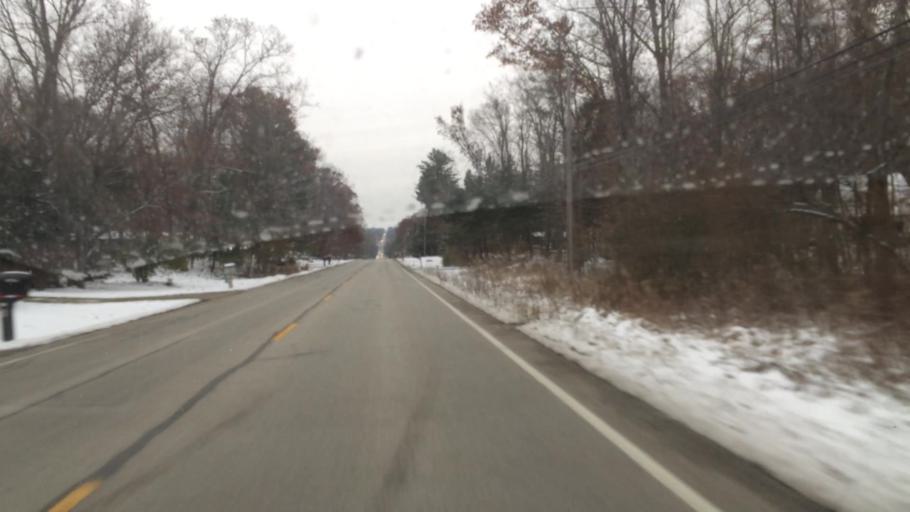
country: US
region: Ohio
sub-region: Cuyahoga County
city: Strongsville
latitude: 41.2974
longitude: -81.7852
